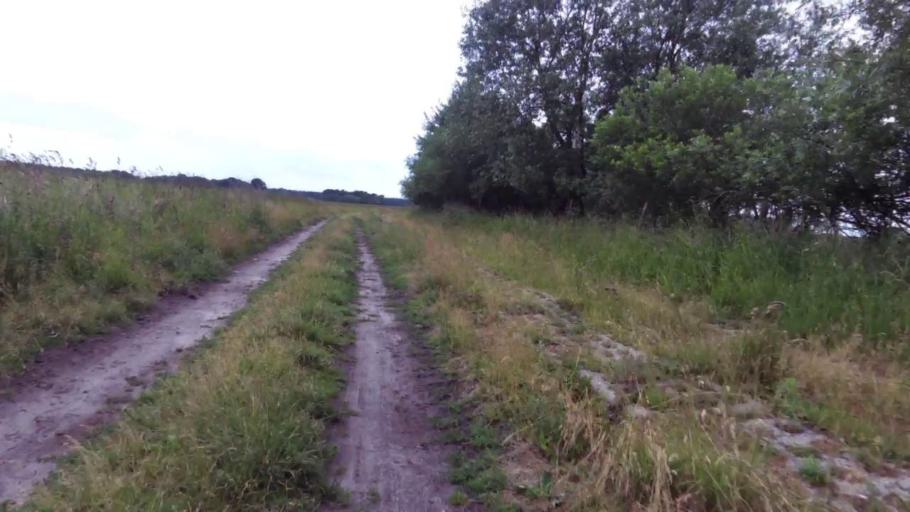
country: PL
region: West Pomeranian Voivodeship
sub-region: Powiat goleniowski
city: Stepnica
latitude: 53.7165
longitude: 14.5713
